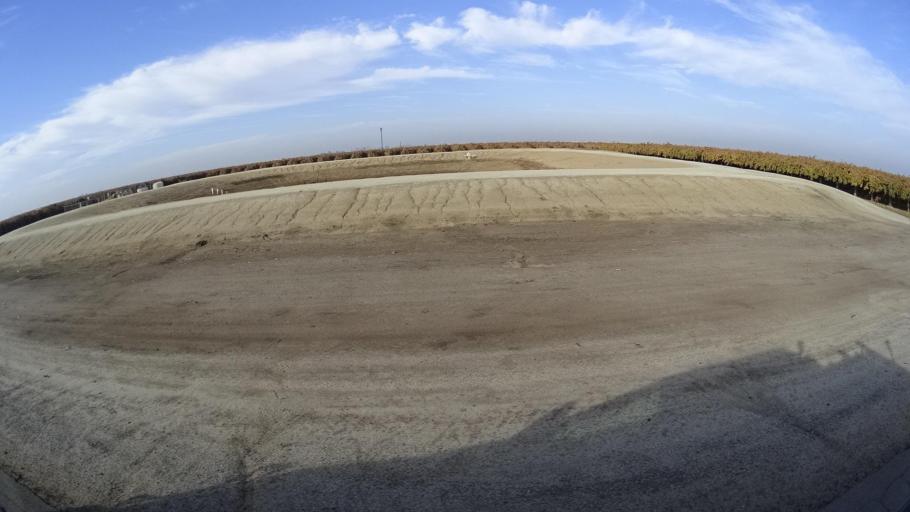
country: US
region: California
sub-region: Kern County
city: McFarland
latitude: 35.7237
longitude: -119.2051
